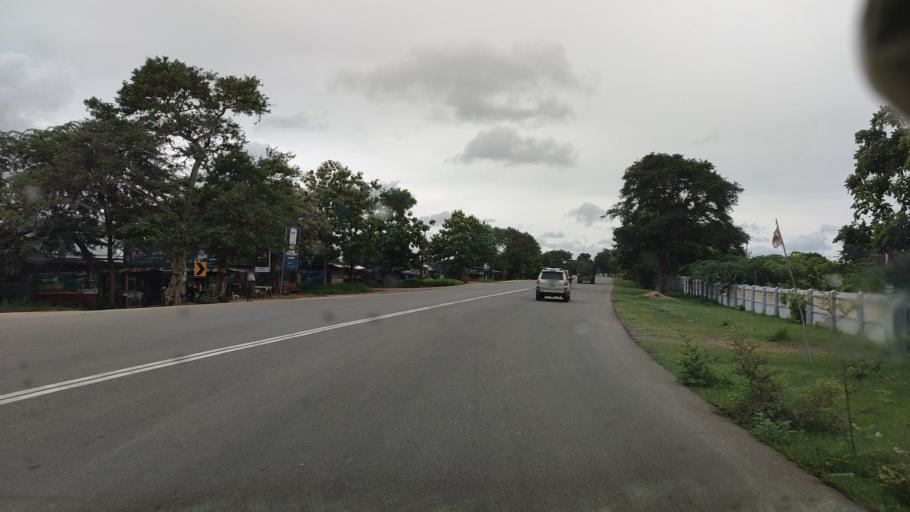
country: MM
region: Mandalay
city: Meiktila
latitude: 20.8353
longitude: 95.8958
